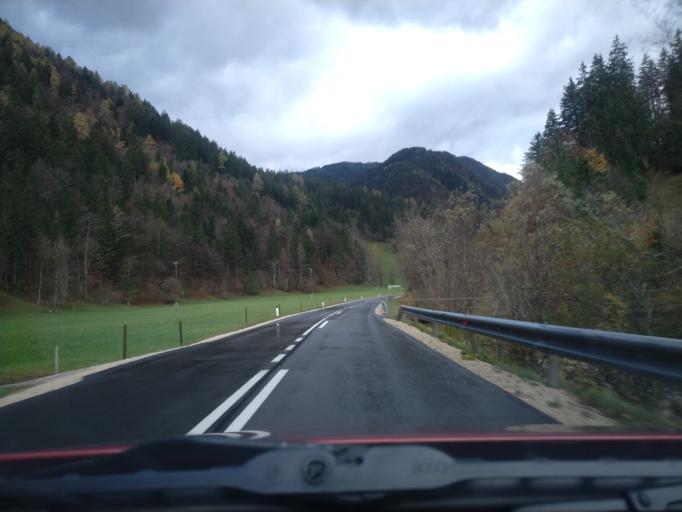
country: SI
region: Solcava
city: Solcava
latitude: 46.3902
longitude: 14.7153
